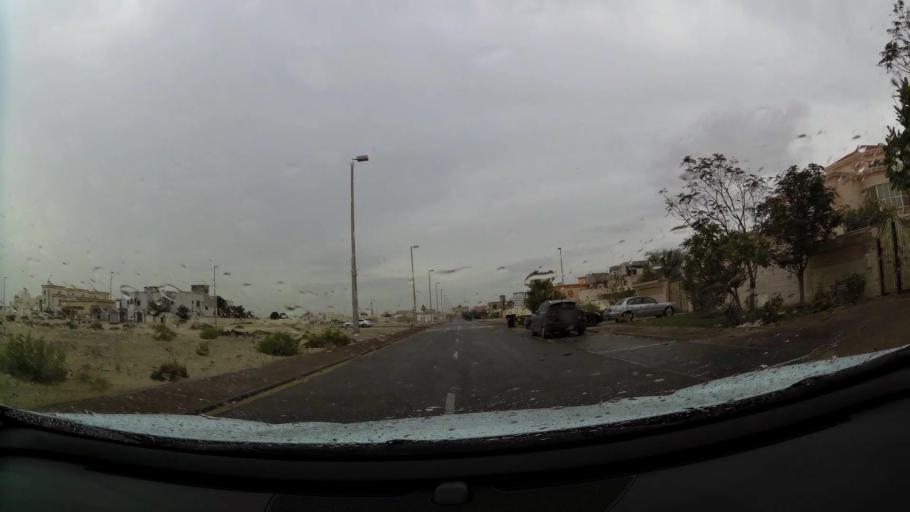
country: AE
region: Abu Dhabi
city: Abu Dhabi
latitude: 24.3646
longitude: 54.6431
